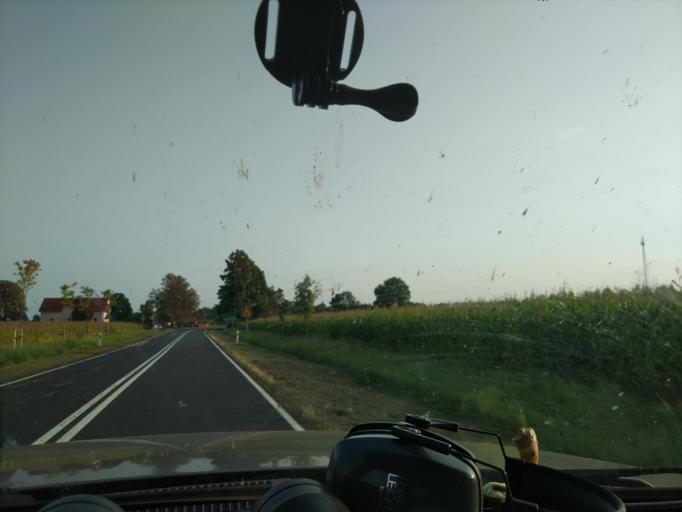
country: PL
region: Warmian-Masurian Voivodeship
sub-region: Powiat szczycienski
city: Wielbark
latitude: 53.3508
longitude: 20.9003
